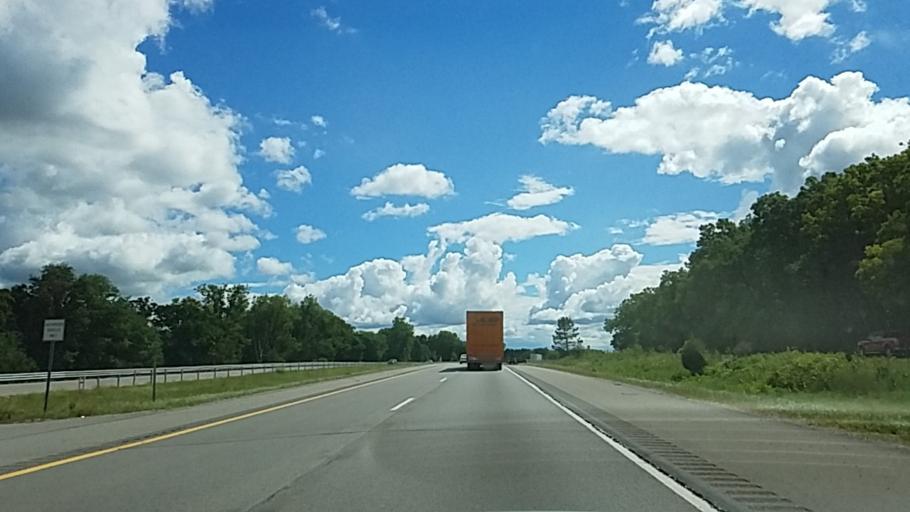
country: US
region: Michigan
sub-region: Livingston County
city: Whitmore Lake
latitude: 42.4802
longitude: -83.7560
